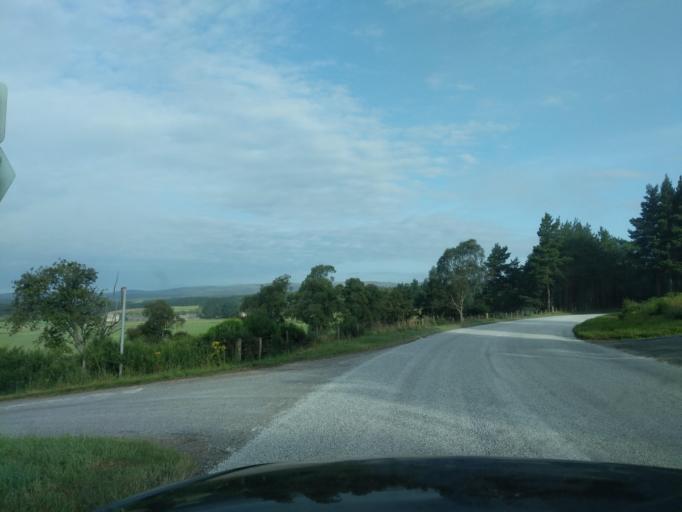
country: GB
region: Scotland
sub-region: Highland
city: Grantown on Spey
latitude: 57.3041
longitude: -3.6980
